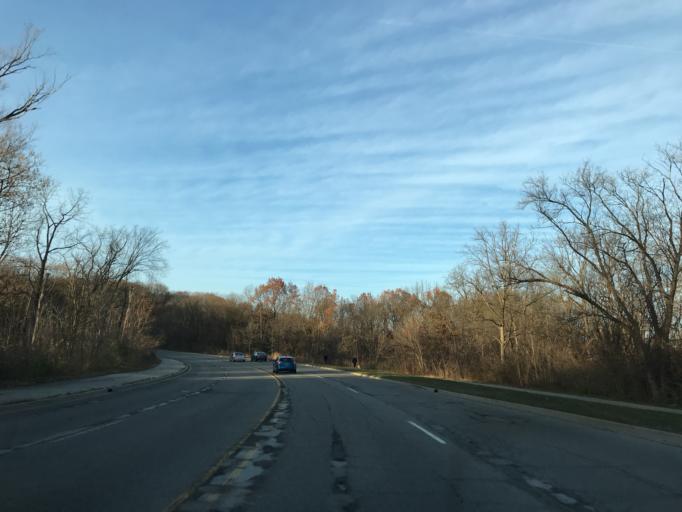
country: US
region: Michigan
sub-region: Washtenaw County
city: Ann Arbor
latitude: 42.2623
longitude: -83.6925
